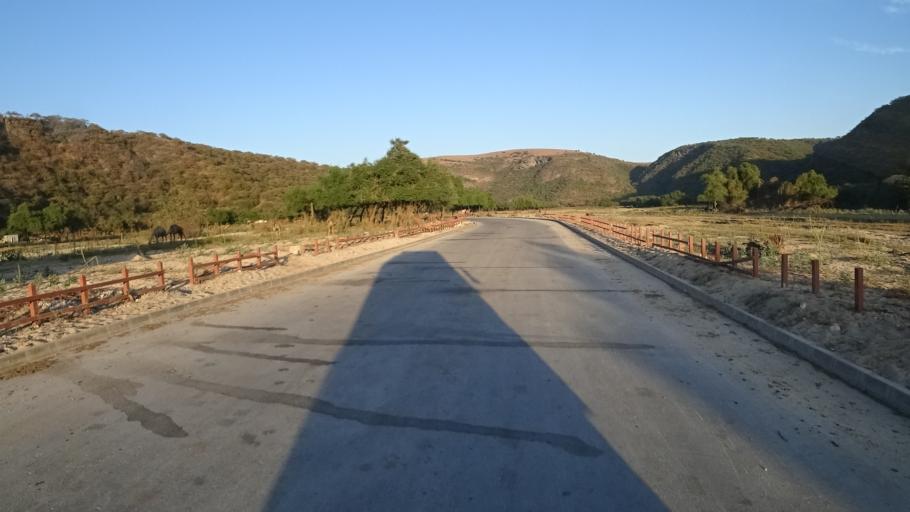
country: OM
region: Zufar
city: Salalah
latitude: 17.0898
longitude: 54.4349
